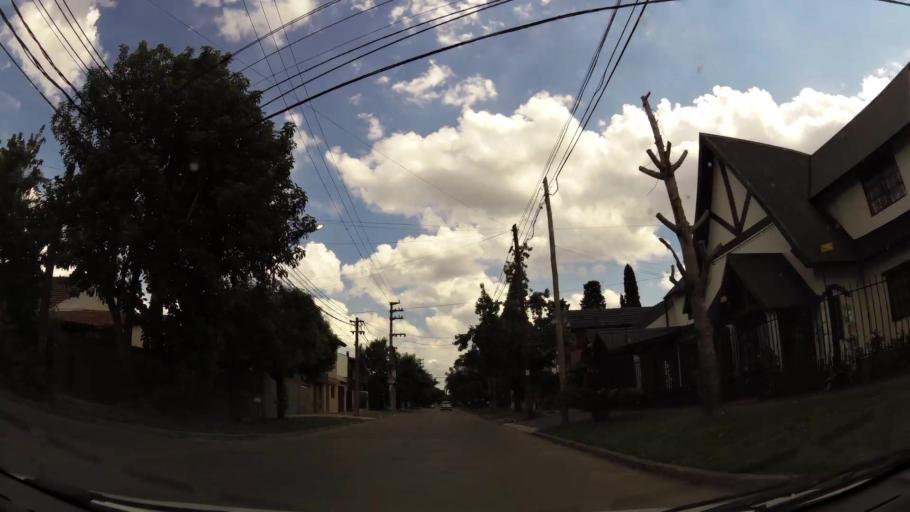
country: AR
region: Buenos Aires
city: Ituzaingo
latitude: -34.6395
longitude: -58.6590
